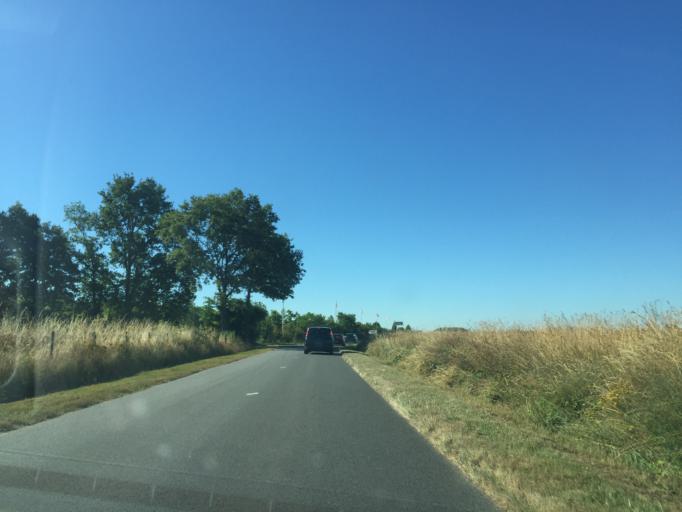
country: FR
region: Auvergne
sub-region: Departement de l'Allier
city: Dompierre-sur-Besbre
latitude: 46.5140
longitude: 3.6223
